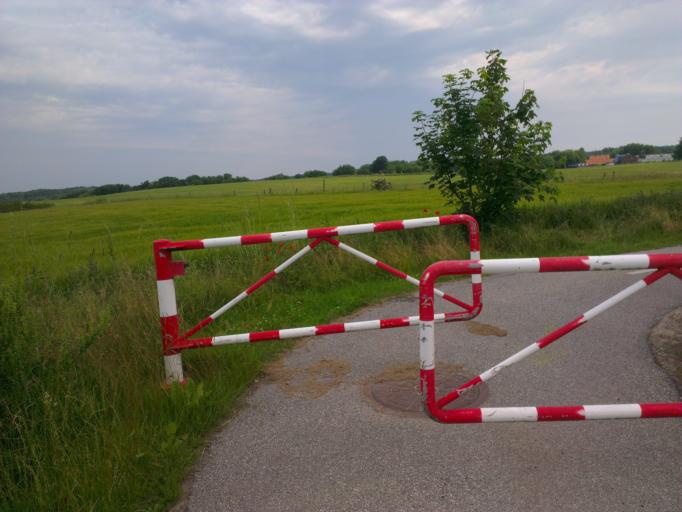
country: DK
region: Capital Region
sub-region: Allerod Kommune
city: Lillerod
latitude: 55.8962
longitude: 12.3253
